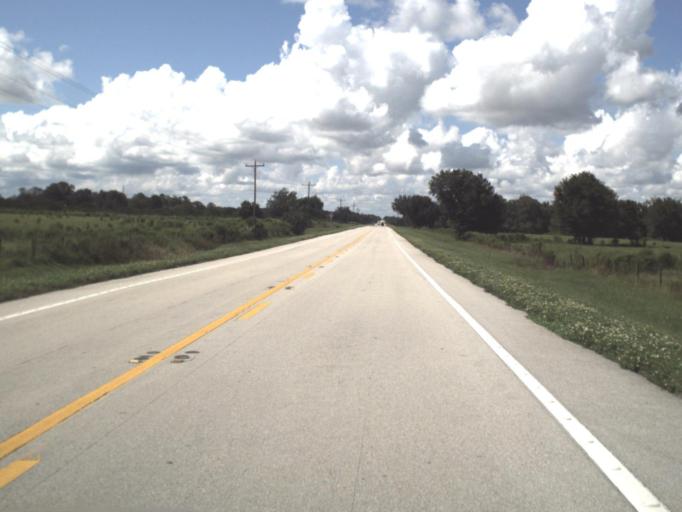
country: US
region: Florida
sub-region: DeSoto County
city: Arcadia
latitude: 27.2512
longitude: -81.9578
